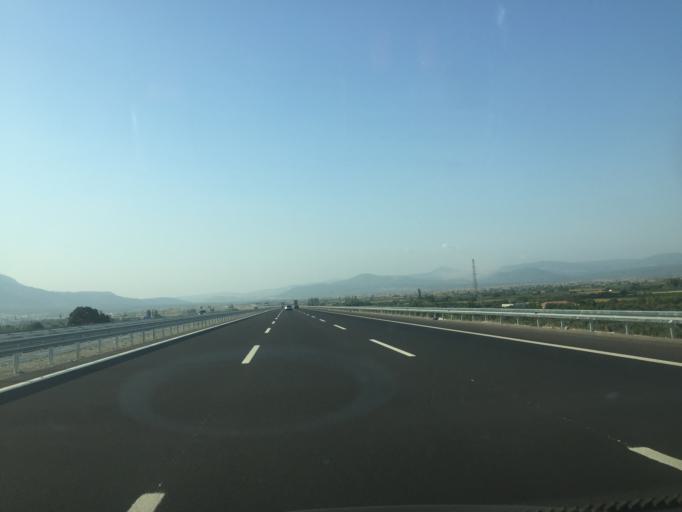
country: TR
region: Manisa
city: Kirkagac
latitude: 39.0749
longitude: 27.7162
